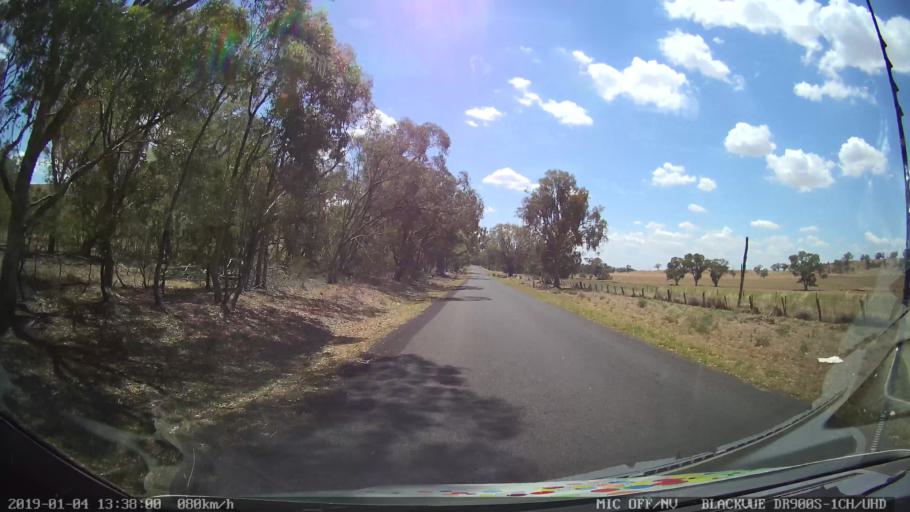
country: AU
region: New South Wales
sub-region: Dubbo Municipality
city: Dubbo
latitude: -32.5433
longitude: 148.5461
